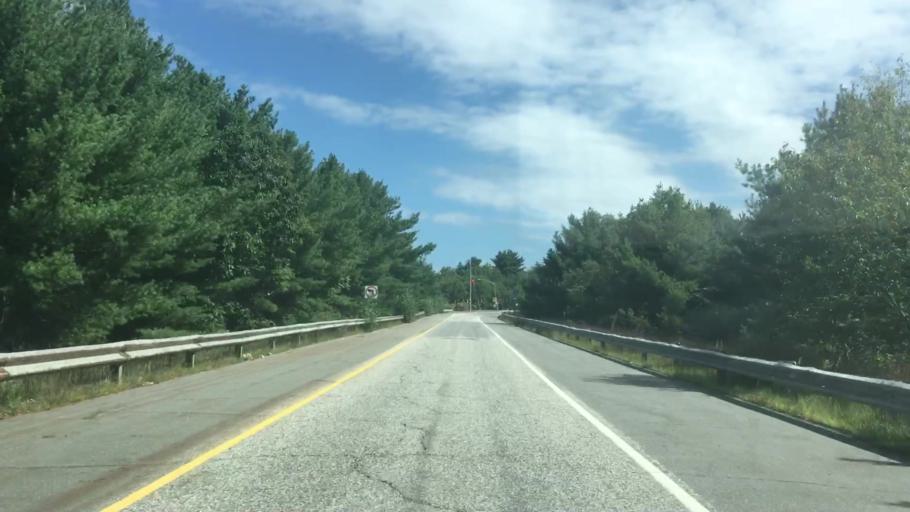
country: US
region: Maine
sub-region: Androscoggin County
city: Lewiston
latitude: 44.0759
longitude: -70.1847
